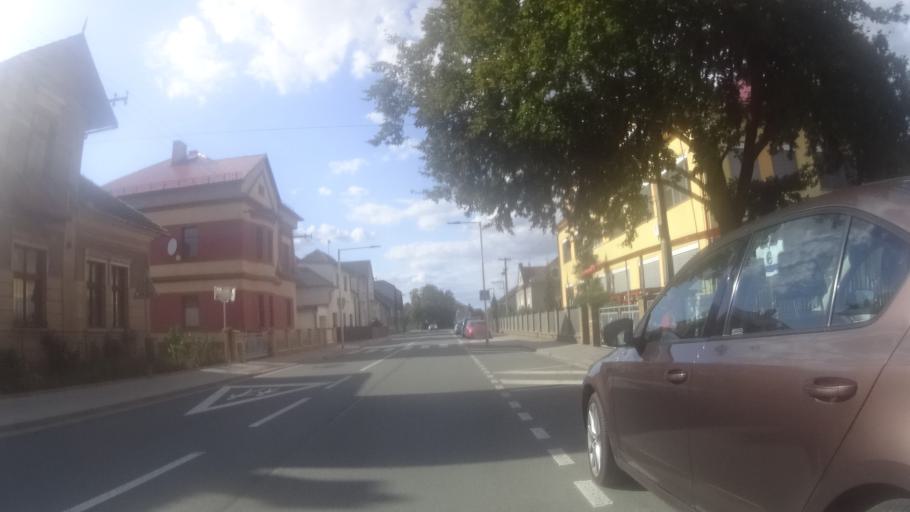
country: CZ
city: Albrechtice nad Orlici
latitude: 50.1409
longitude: 16.0632
